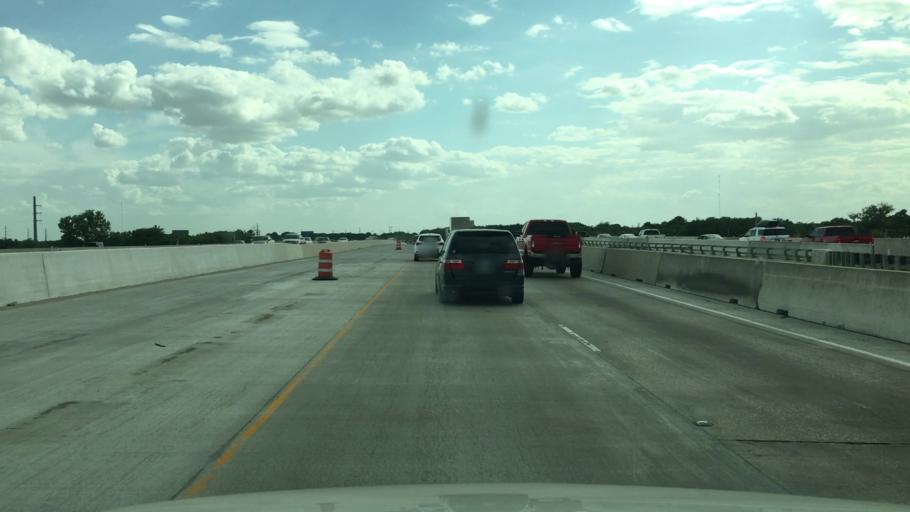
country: US
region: Texas
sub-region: McLennan County
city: Bruceville-Eddy
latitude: 31.3212
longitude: -97.2343
